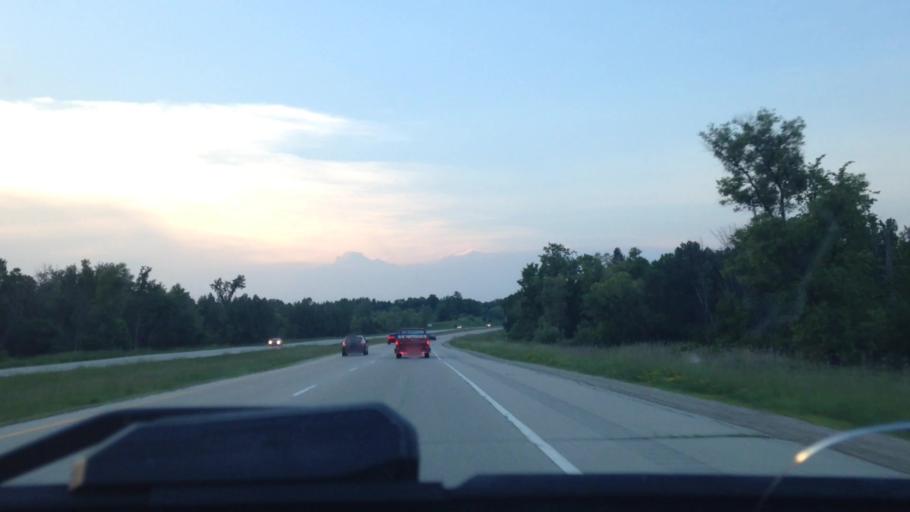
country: US
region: Wisconsin
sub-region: Washington County
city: Jackson
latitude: 43.3666
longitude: -88.1931
